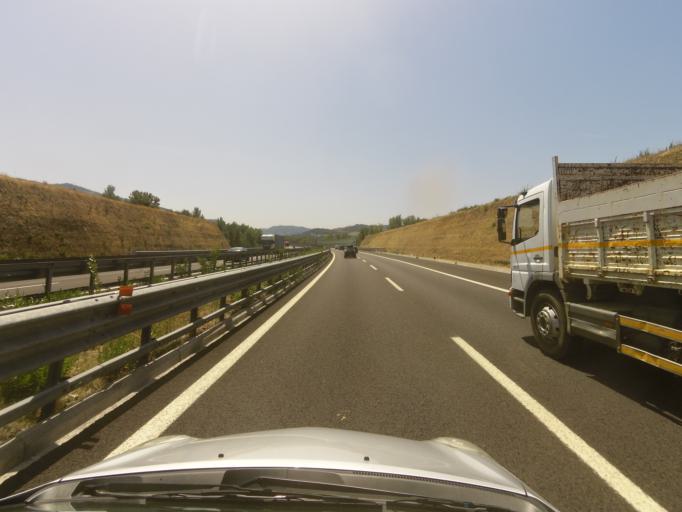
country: IT
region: Emilia-Romagna
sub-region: Provincia di Bologna
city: Grizzana
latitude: 44.2679
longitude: 11.1879
